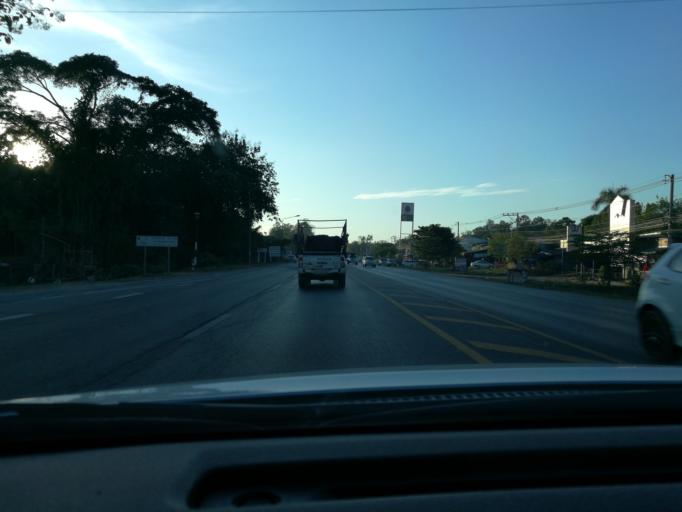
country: TH
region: Phitsanulok
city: Wang Thong
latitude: 16.8430
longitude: 100.5422
